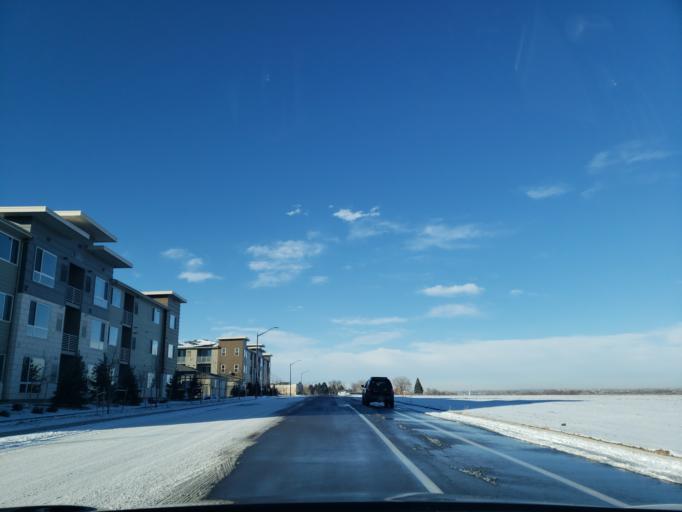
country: US
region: Colorado
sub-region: Larimer County
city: Fort Collins
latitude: 40.5180
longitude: -105.0072
